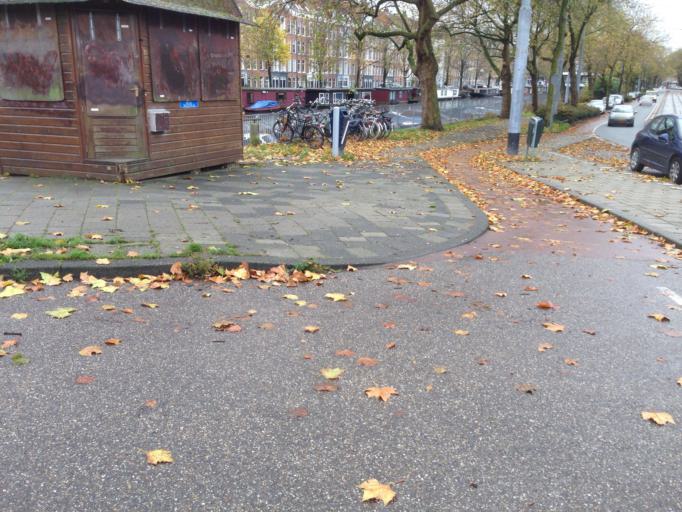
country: NL
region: North Holland
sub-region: Gemeente Amsterdam
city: Amsterdam
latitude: 52.3815
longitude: 4.8795
